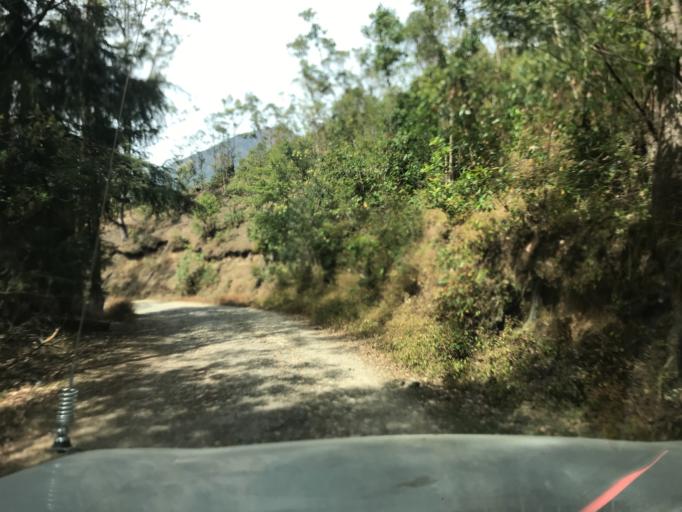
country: TL
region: Ainaro
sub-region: Ainaro
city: Ainaro
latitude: -8.8821
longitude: 125.5279
